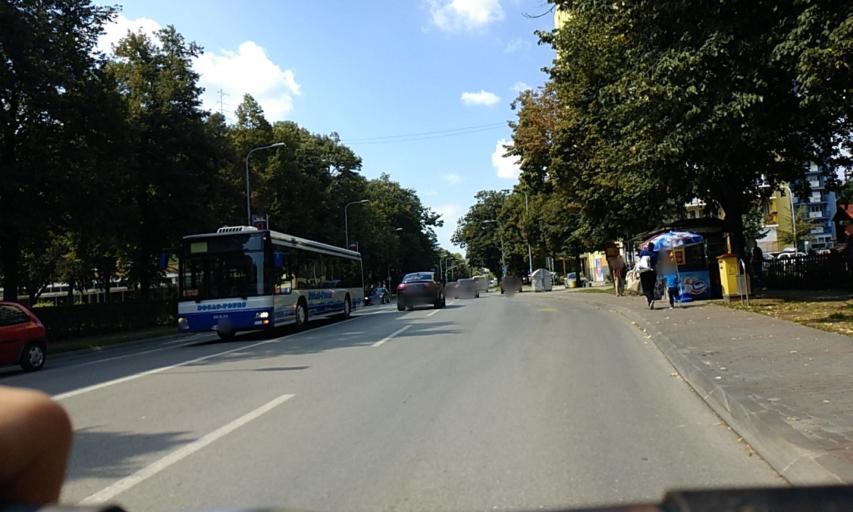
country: BA
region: Republika Srpska
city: Banja Luka
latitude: 44.7691
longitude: 17.1864
